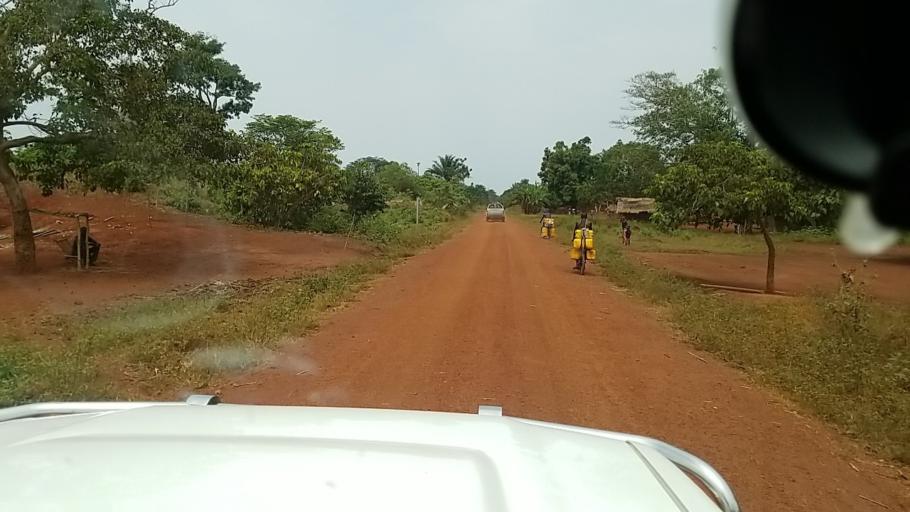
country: CD
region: Equateur
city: Gemena
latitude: 3.5223
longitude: 19.3647
